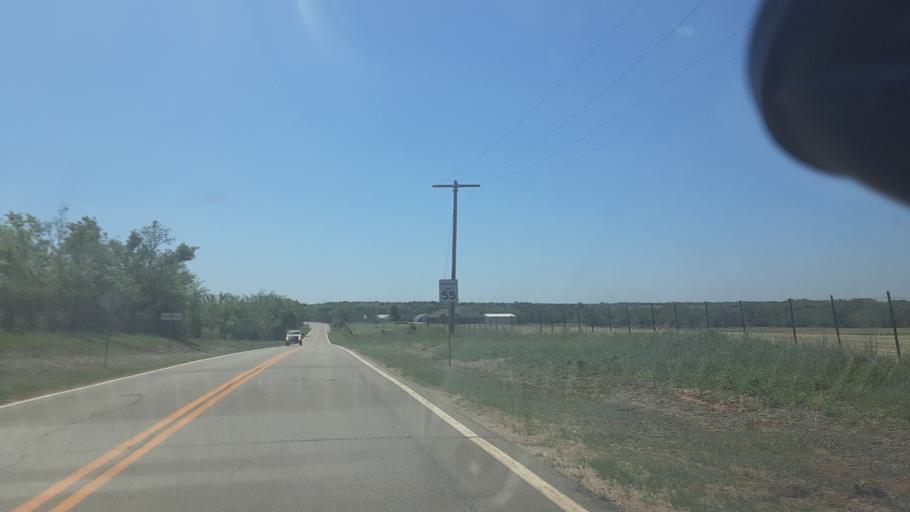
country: US
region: Oklahoma
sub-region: Logan County
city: Guthrie
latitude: 36.0576
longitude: -97.4075
